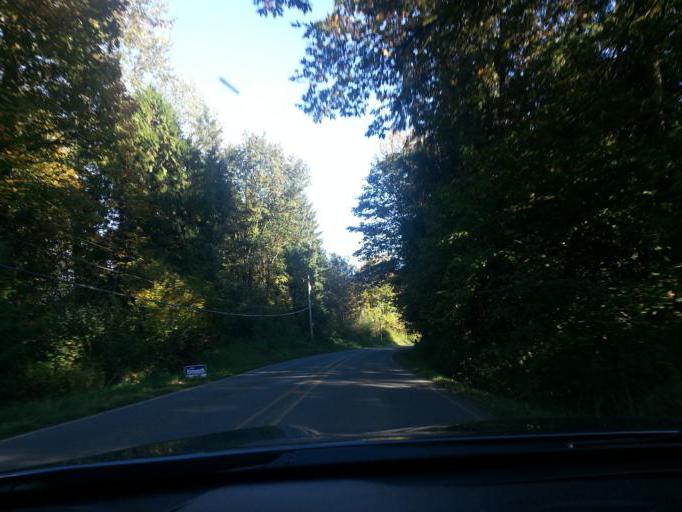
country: US
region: Washington
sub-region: Snohomish County
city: Cathcart
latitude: 47.8774
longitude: -122.1069
